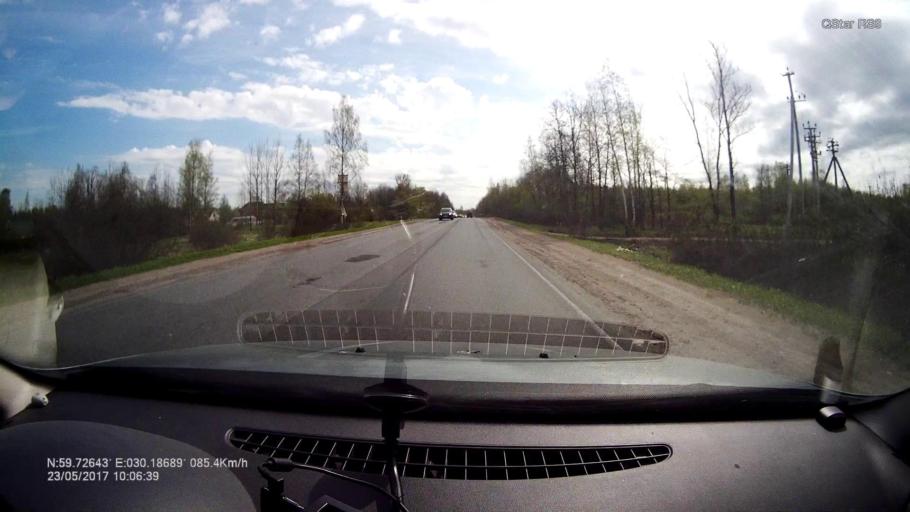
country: RU
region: St.-Petersburg
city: Gorelovo
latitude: 59.7263
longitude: 30.1880
